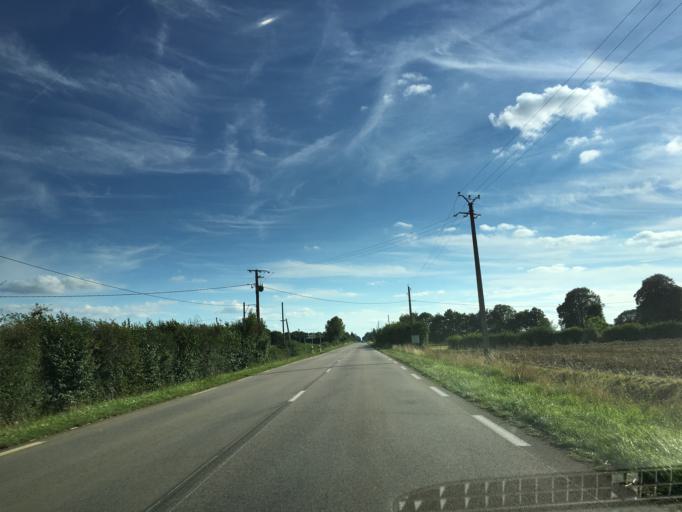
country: FR
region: Lower Normandy
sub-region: Departement du Calvados
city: Orbec
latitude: 48.9183
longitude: 0.4272
